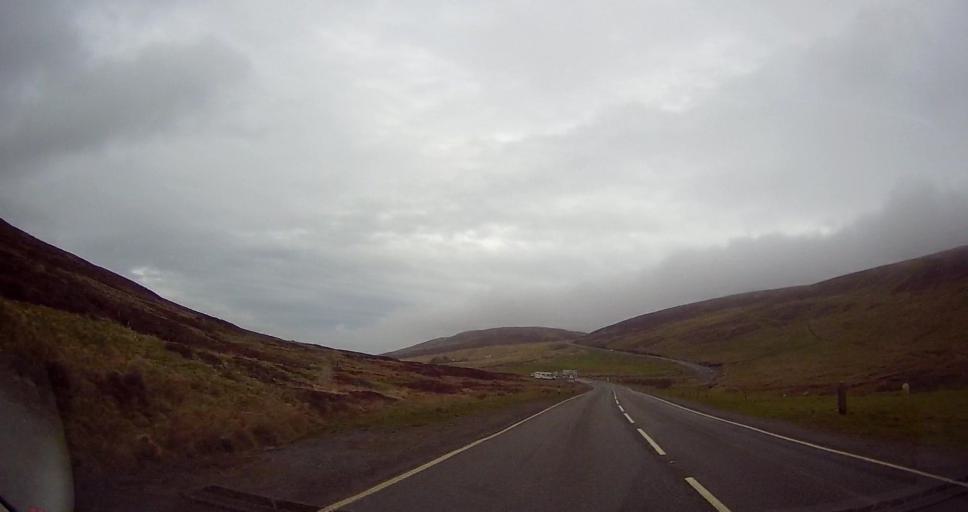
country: GB
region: Scotland
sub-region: Shetland Islands
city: Lerwick
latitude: 60.1591
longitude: -1.2311
